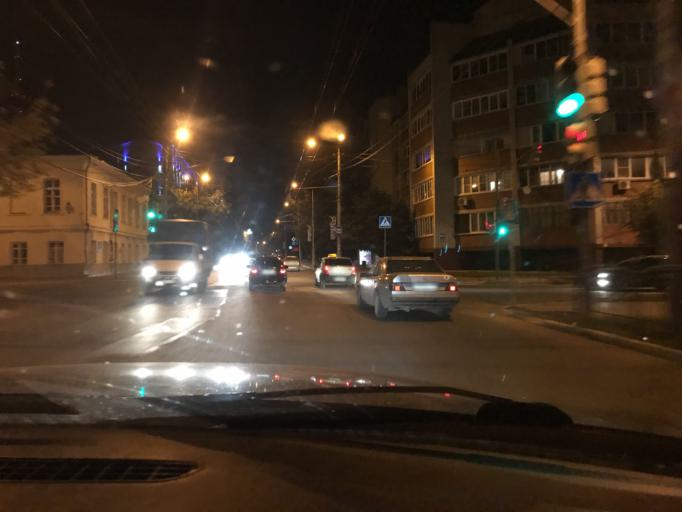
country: RU
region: Kaluga
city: Kaluga
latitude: 54.5177
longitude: 36.2630
